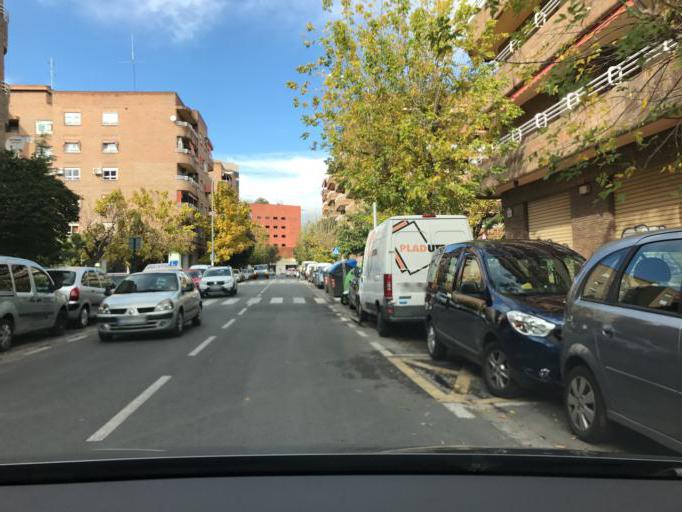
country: ES
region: Andalusia
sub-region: Provincia de Granada
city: Granada
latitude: 37.1648
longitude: -3.6059
